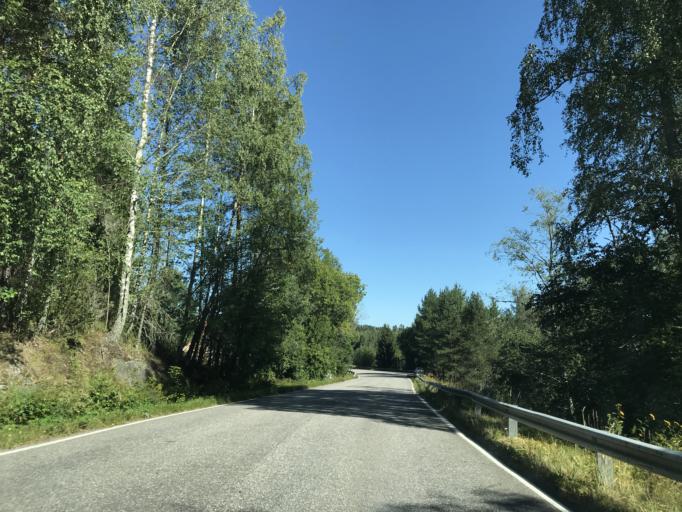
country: FI
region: Paijanne Tavastia
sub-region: Lahti
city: Orimattila
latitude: 60.7964
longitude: 25.6926
